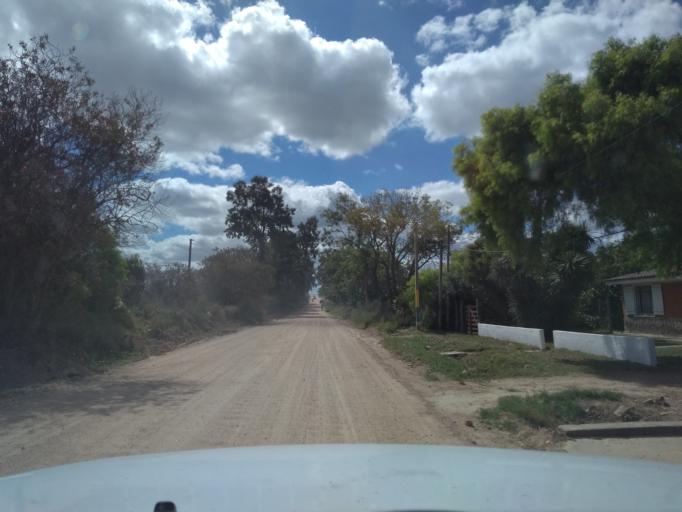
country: UY
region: Canelones
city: Colonia Nicolich
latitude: -34.8328
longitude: -55.9884
